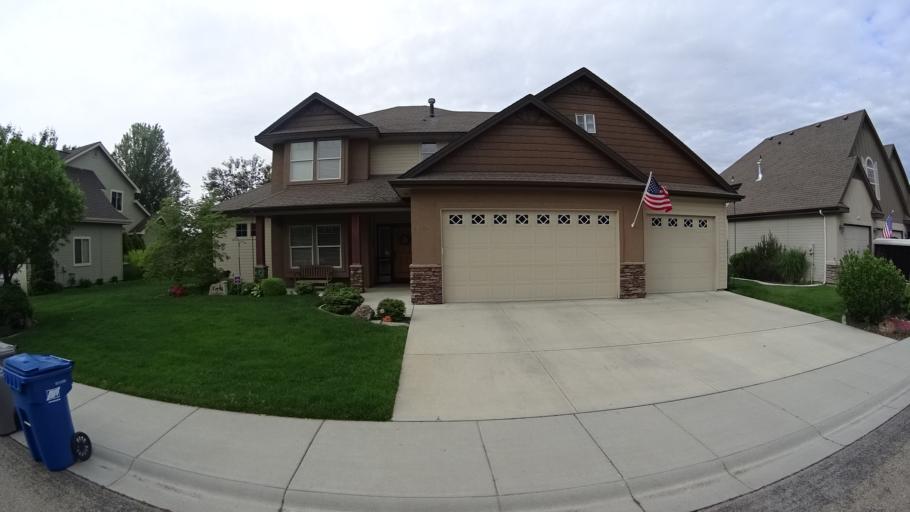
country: US
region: Idaho
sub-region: Ada County
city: Star
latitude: 43.6882
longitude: -116.5031
